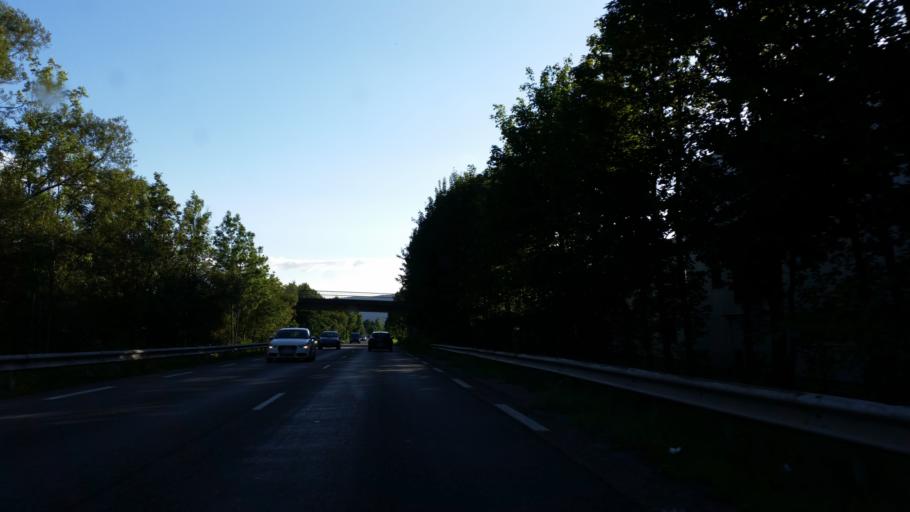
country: FR
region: Lorraine
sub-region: Departement des Vosges
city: Saint-Ame
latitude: 48.0184
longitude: 6.6688
